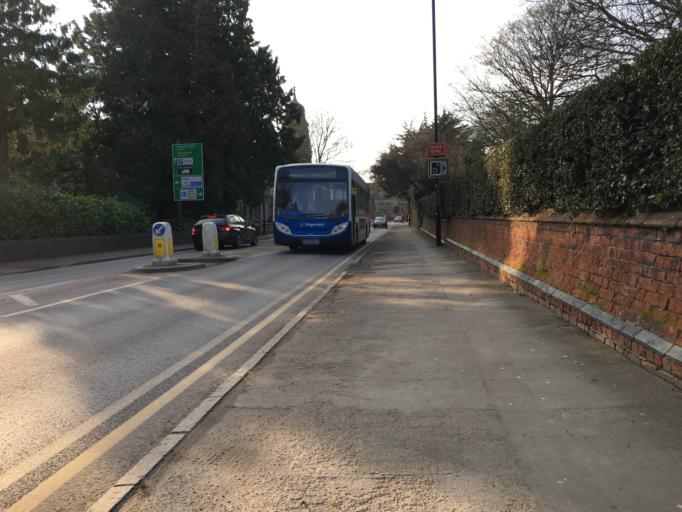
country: GB
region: England
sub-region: Warwickshire
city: Rugby
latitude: 52.3703
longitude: -1.2600
